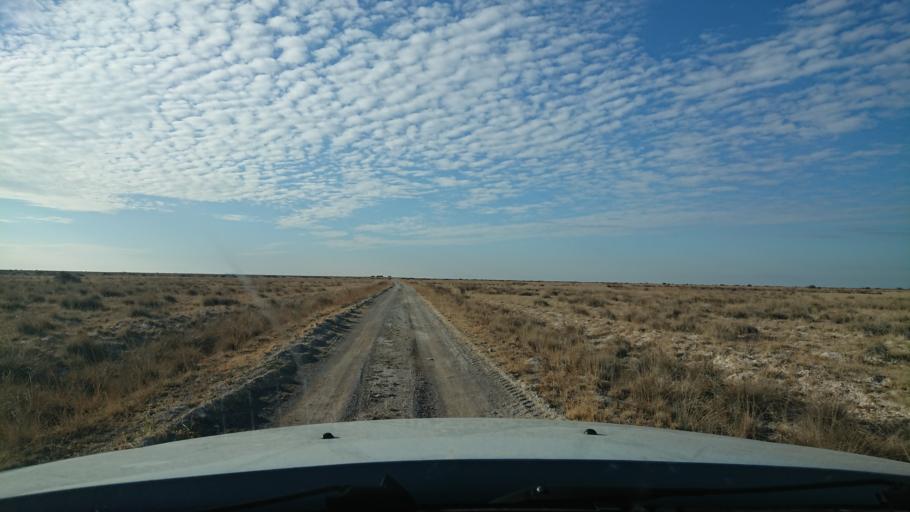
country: TR
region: Aksaray
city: Eskil
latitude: 38.5423
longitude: 33.3323
